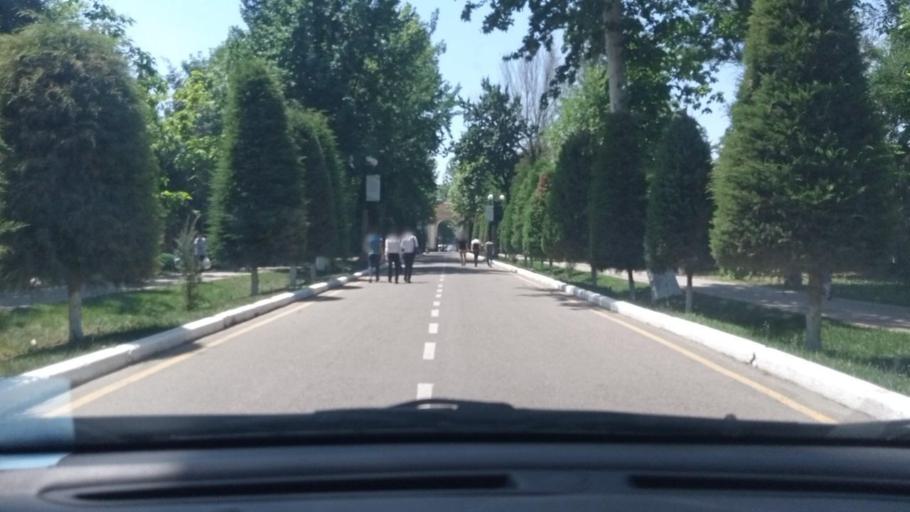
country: UZ
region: Toshkent Shahri
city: Tashkent
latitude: 41.2750
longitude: 69.2798
